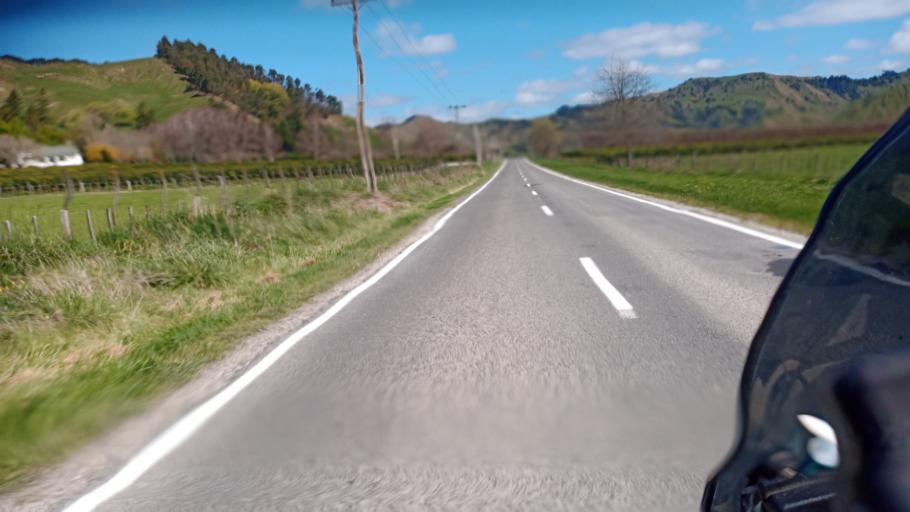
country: NZ
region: Gisborne
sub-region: Gisborne District
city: Gisborne
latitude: -38.7057
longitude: 177.8429
